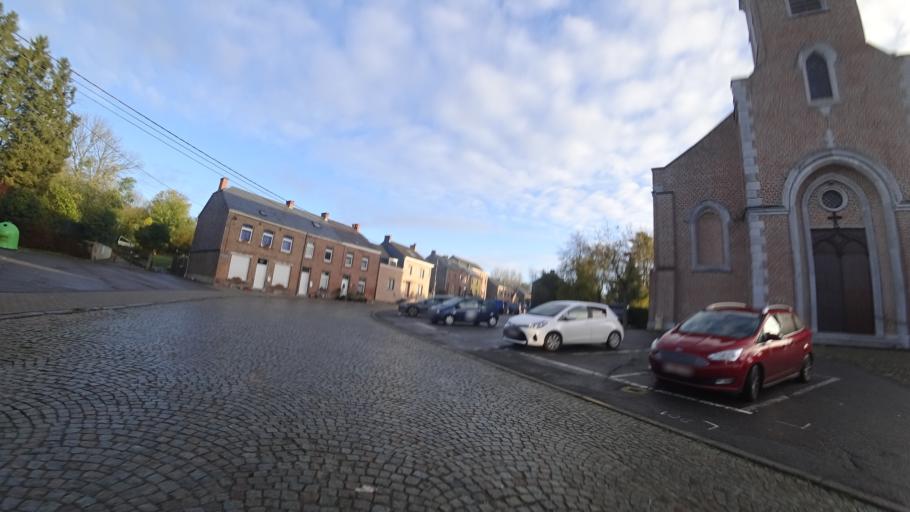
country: BE
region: Wallonia
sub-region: Province de Namur
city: Gembloux
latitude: 50.5531
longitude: 4.7264
